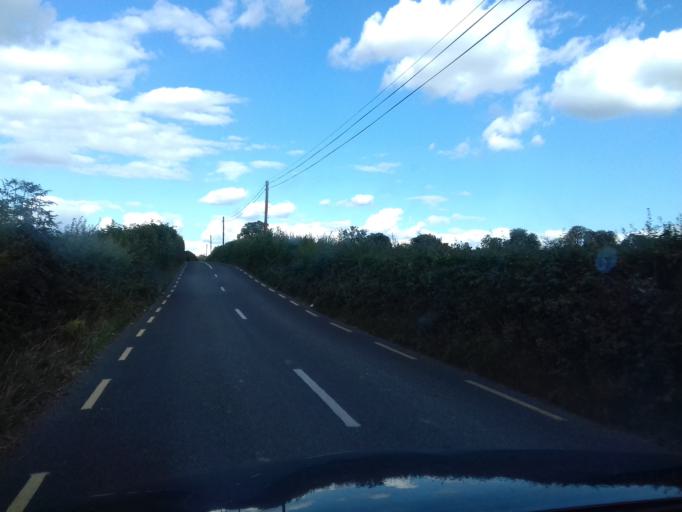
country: IE
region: Leinster
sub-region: Kilkenny
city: Thomastown
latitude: 52.5329
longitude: -7.1126
